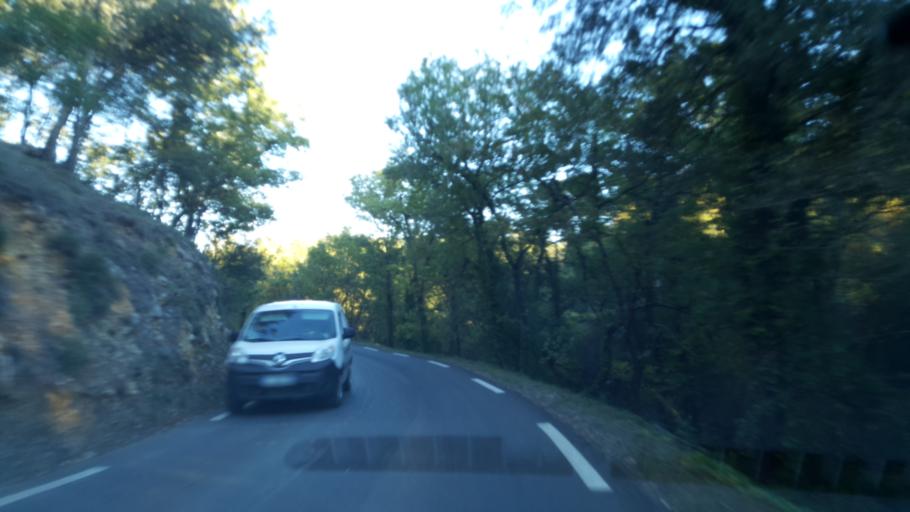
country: FR
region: Provence-Alpes-Cote d'Azur
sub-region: Departement du Var
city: Barjols
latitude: 43.5871
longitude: 5.9559
